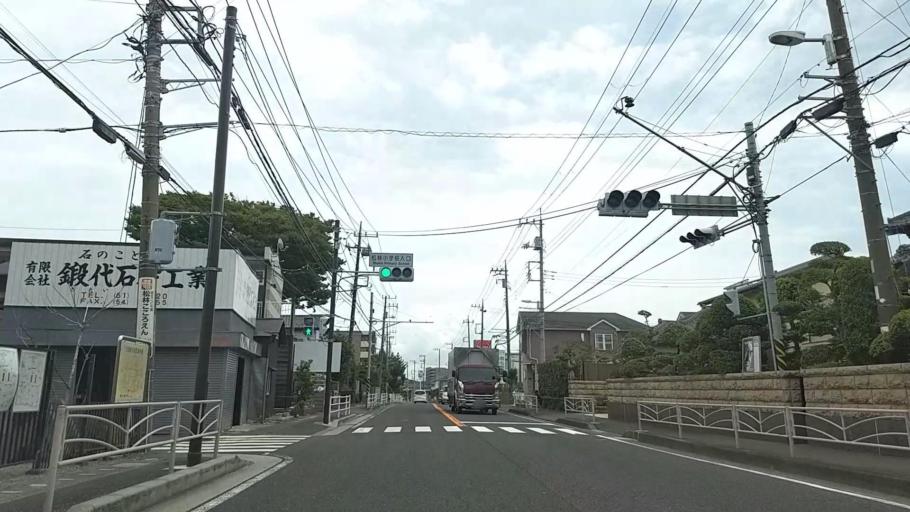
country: JP
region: Kanagawa
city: Chigasaki
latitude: 35.3374
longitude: 139.4263
